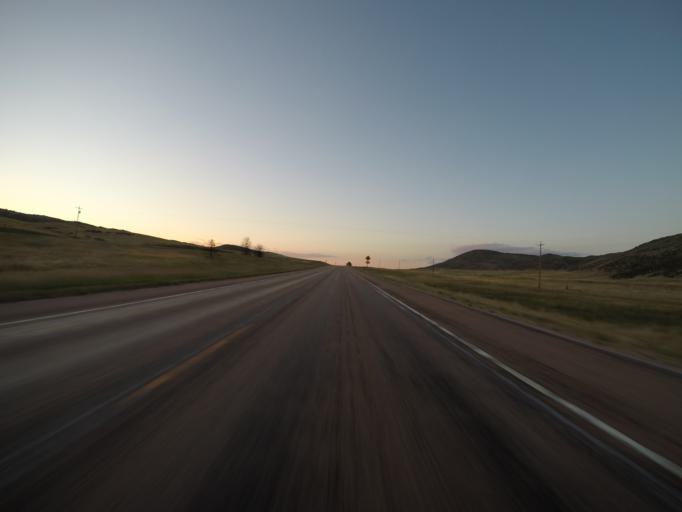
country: US
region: Colorado
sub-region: Larimer County
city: Laporte
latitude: 40.7392
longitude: -105.1709
